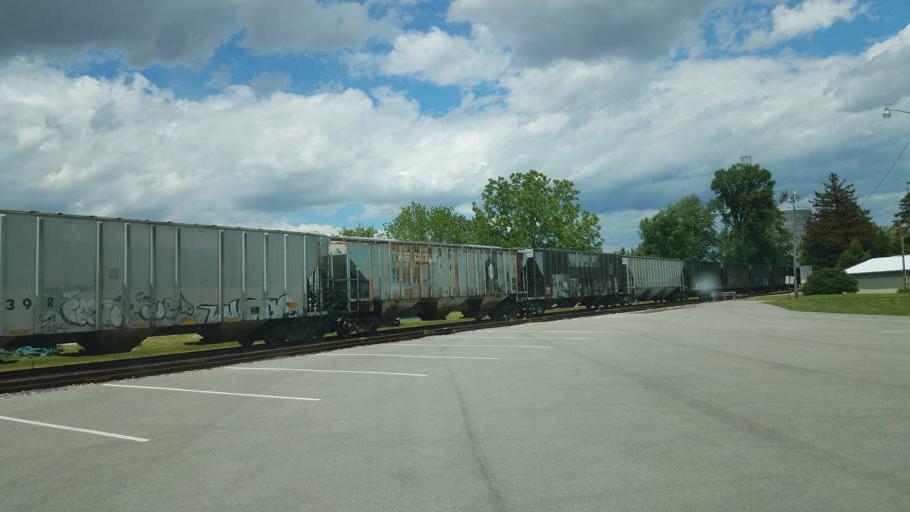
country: US
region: Ohio
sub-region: Huron County
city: Monroeville
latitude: 41.2432
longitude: -82.7009
